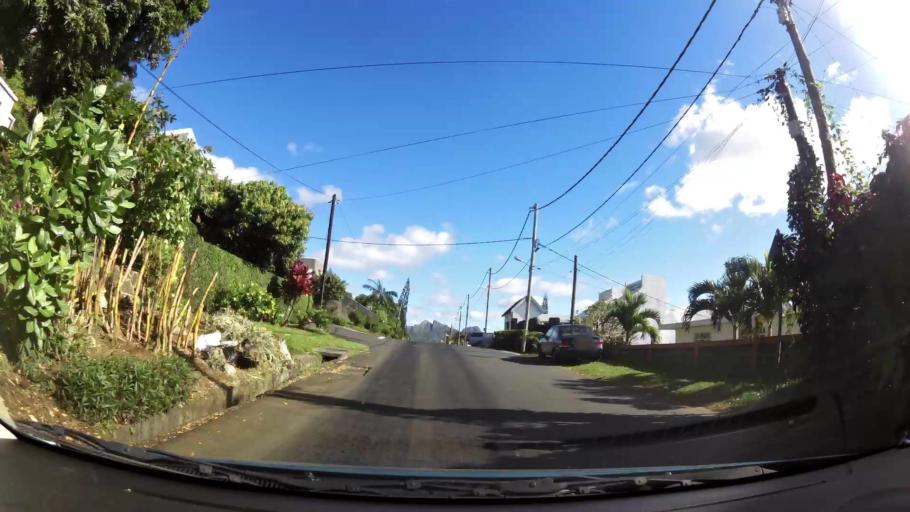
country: MU
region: Plaines Wilhems
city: Quatre Bornes
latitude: -20.2733
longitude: 57.4816
